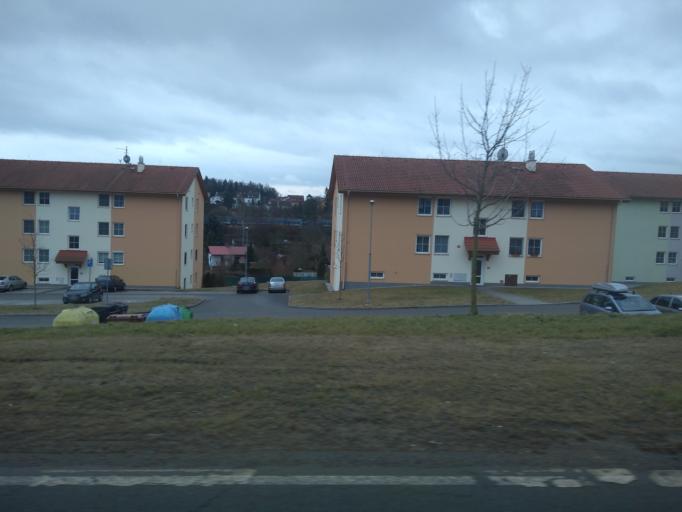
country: CZ
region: Plzensky
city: Vejprnice
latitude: 49.7324
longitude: 13.2854
